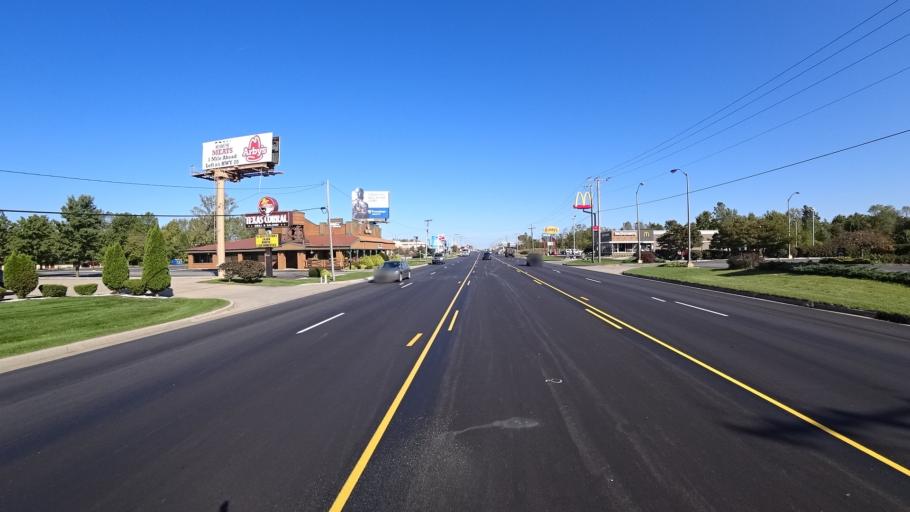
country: US
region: Indiana
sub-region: LaPorte County
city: Michigan City
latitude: 41.6668
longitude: -86.8941
